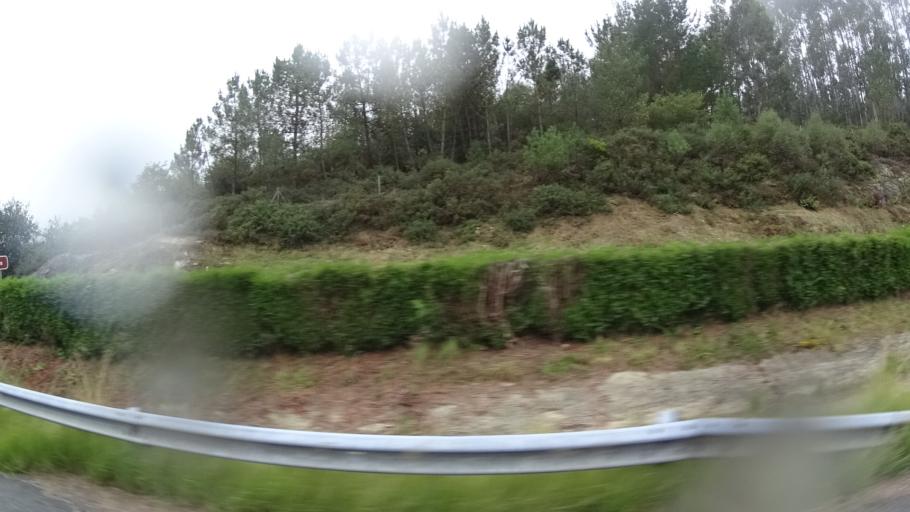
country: ES
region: Galicia
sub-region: Provincia de Lugo
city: Guitiriz
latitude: 43.1823
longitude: -7.8162
